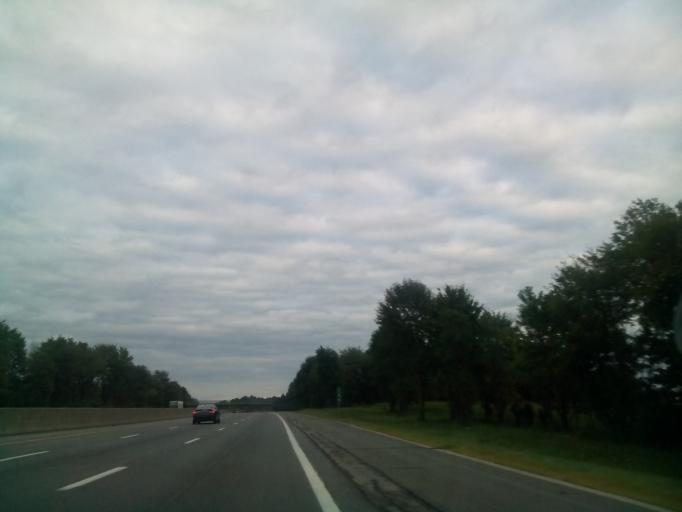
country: US
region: Ohio
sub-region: Portage County
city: Garrettsville
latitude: 41.2423
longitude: -81.1392
